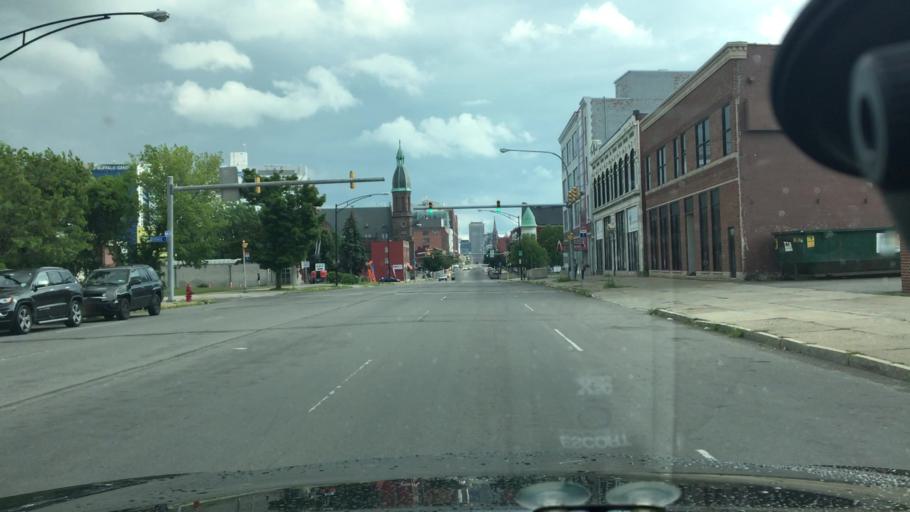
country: US
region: New York
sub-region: Erie County
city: Buffalo
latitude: 42.9063
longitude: -78.8677
